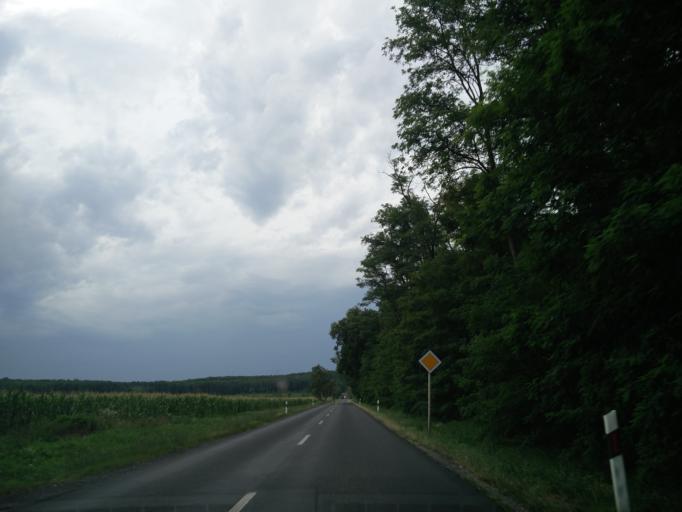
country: HU
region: Vas
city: Vasvar
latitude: 47.0156
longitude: 16.8235
